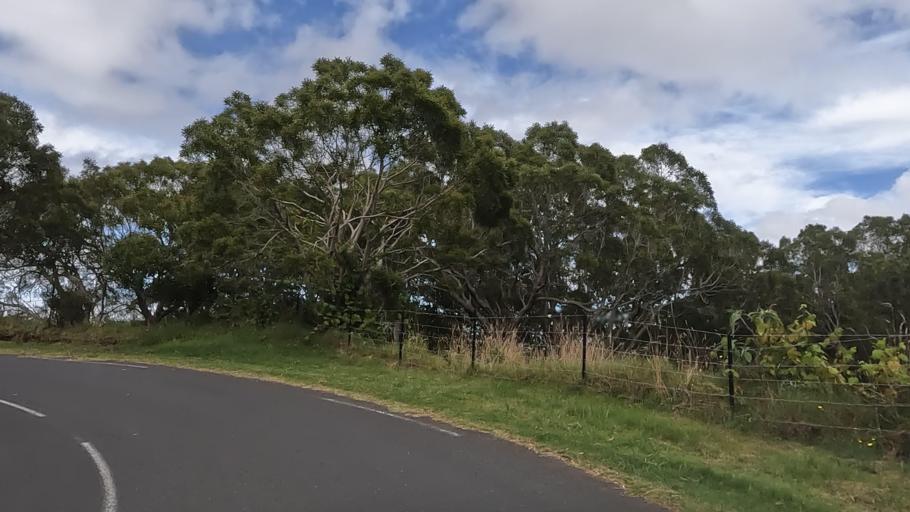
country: RE
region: Reunion
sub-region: Reunion
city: Le Tampon
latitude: -21.2434
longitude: 55.5875
